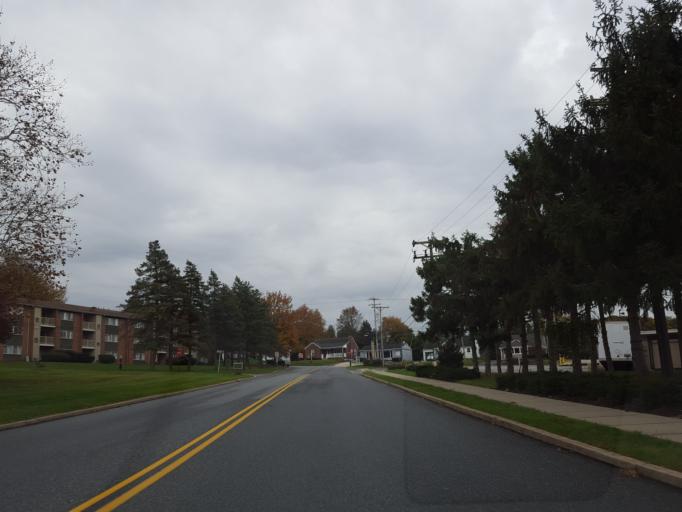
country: US
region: Pennsylvania
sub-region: York County
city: Valley View
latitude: 39.9396
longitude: -76.6905
